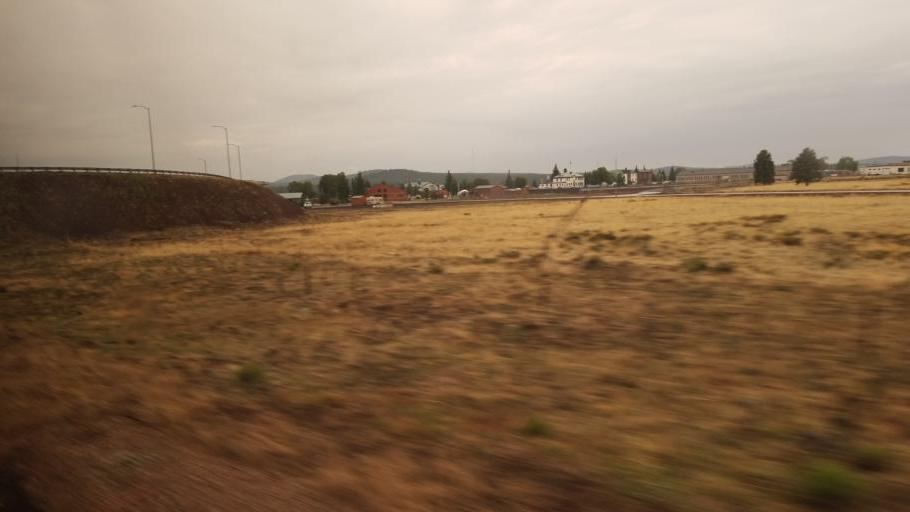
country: US
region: Arizona
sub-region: Coconino County
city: Parks
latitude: 35.2326
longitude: -111.8234
